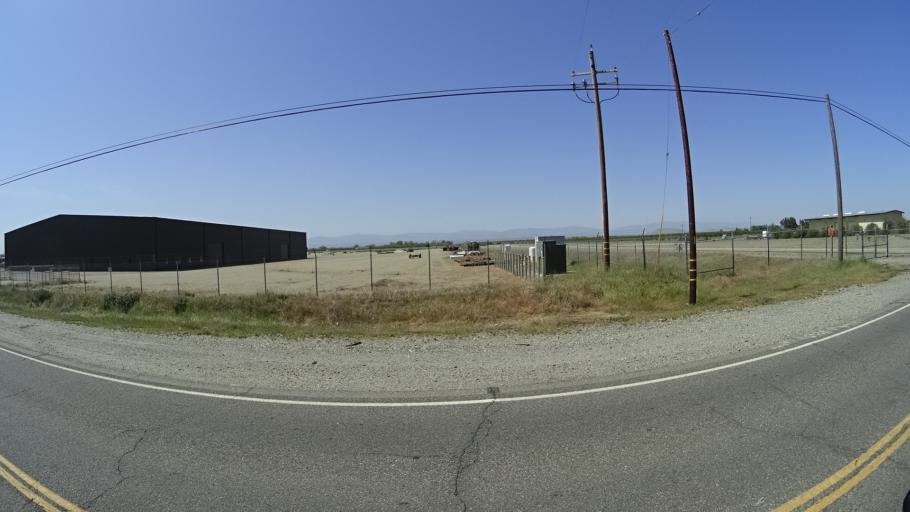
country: US
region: California
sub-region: Glenn County
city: Orland
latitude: 39.6895
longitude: -122.1967
